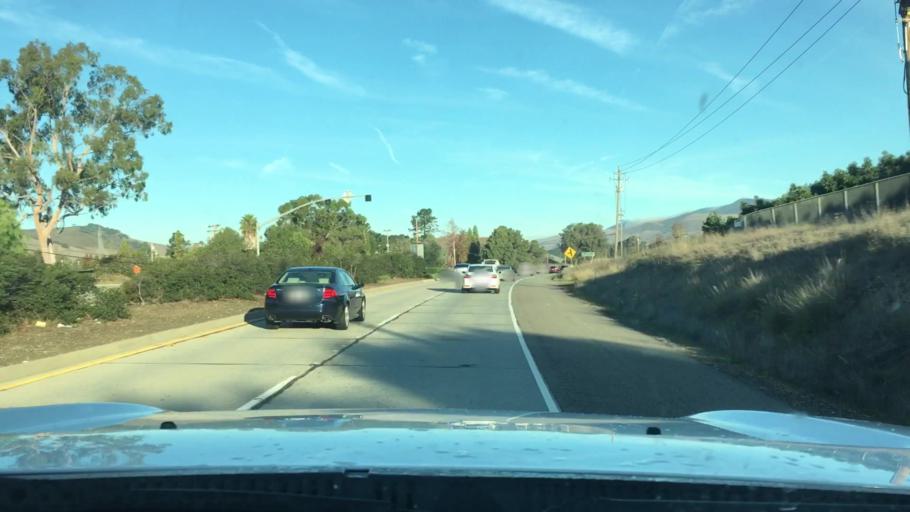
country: US
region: California
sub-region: San Luis Obispo County
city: San Luis Obispo
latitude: 35.2999
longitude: -120.6751
